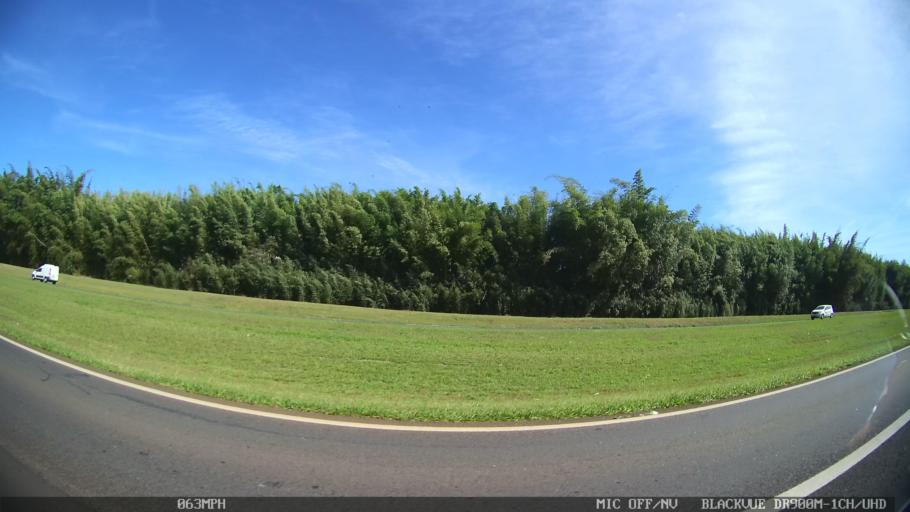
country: BR
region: Sao Paulo
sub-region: Araras
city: Araras
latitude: -22.2779
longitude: -47.3927
